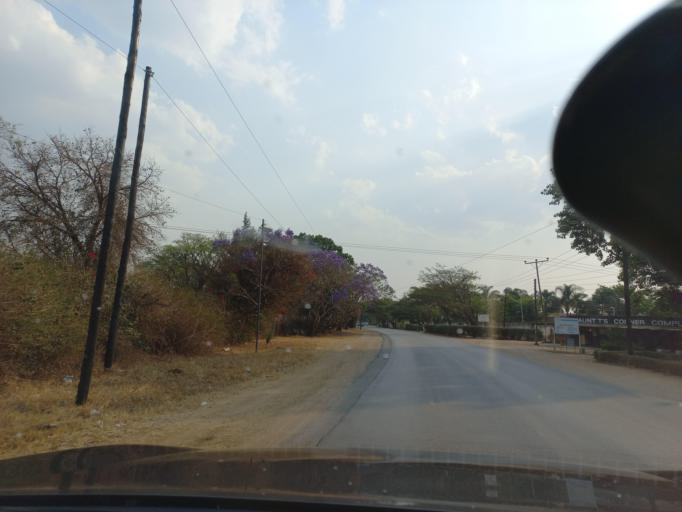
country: ZM
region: Lusaka
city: Lusaka
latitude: -15.4695
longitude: 28.2232
